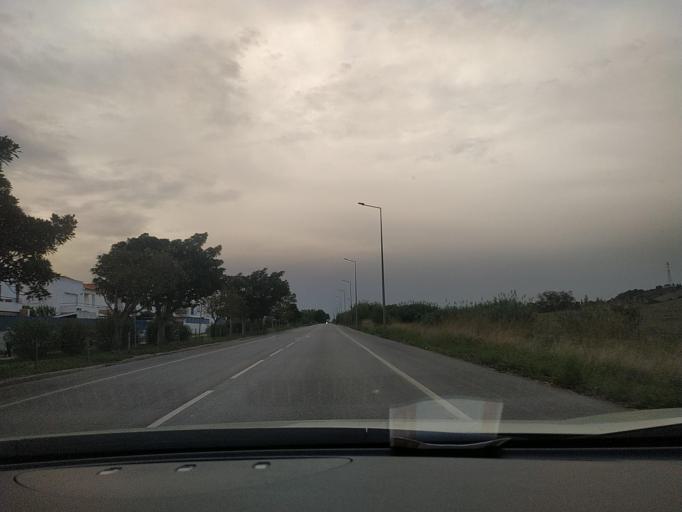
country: PT
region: Lisbon
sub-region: Loures
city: Santa Iria da Azoia
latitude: 38.8671
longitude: -9.0935
